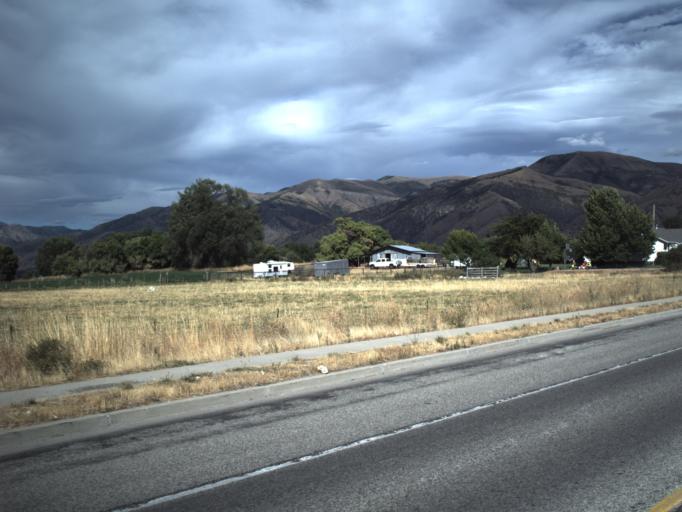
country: US
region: Utah
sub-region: Cache County
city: Hyrum
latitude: 41.6407
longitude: -111.8729
